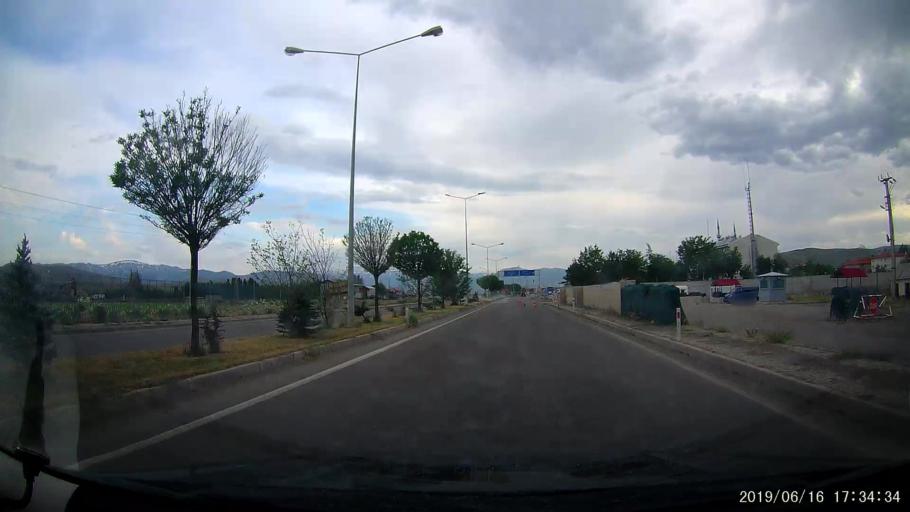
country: TR
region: Erzincan
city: Tercan
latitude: 39.7405
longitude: 40.2678
